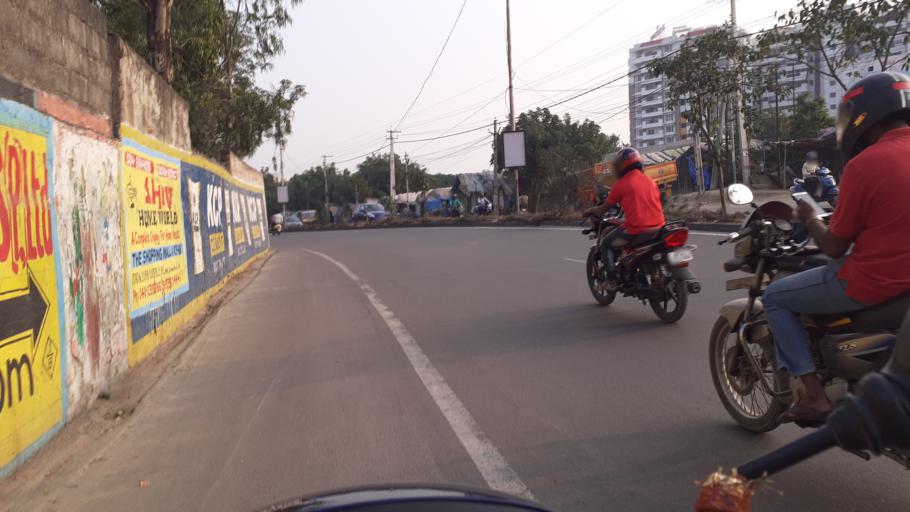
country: IN
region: Telangana
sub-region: Medak
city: Serilingampalle
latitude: 17.4895
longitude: 78.3543
